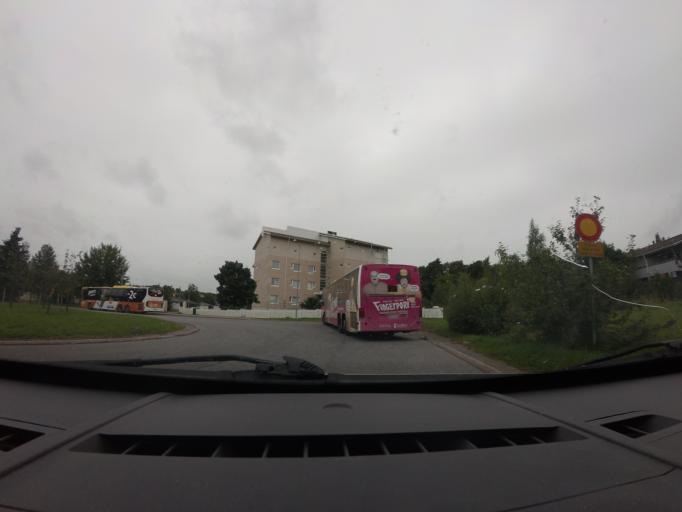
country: FI
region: Varsinais-Suomi
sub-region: Turku
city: Turku
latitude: 60.4133
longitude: 22.2893
